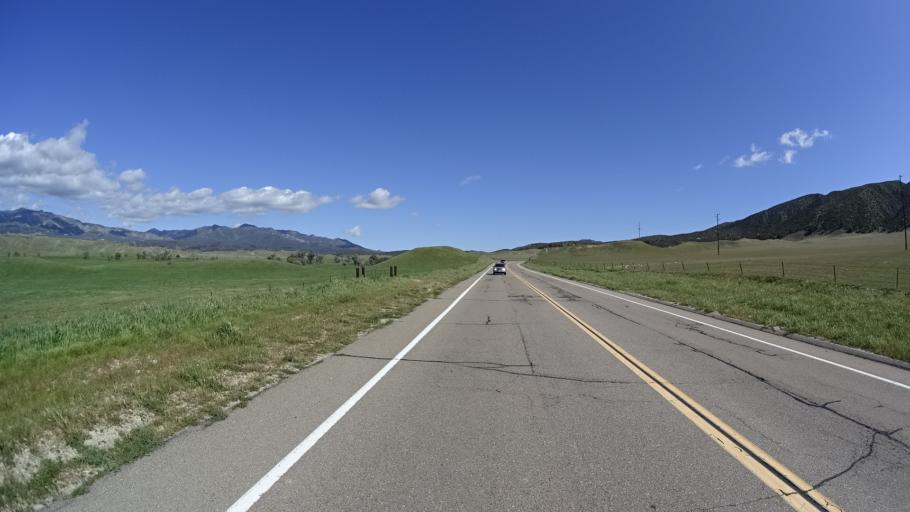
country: US
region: California
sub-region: San Diego County
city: Julian
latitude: 33.2306
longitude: -116.6333
